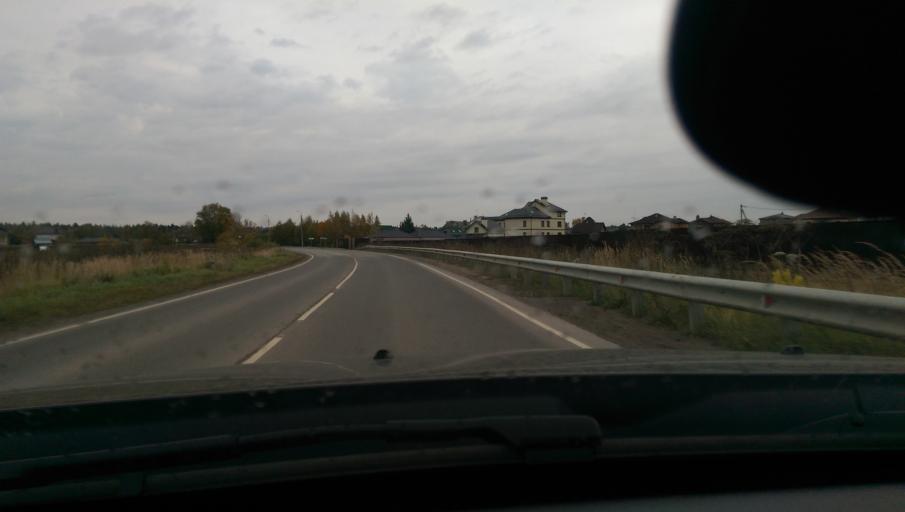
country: RU
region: Moskovskaya
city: Pirogovskiy
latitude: 56.0085
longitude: 37.7220
